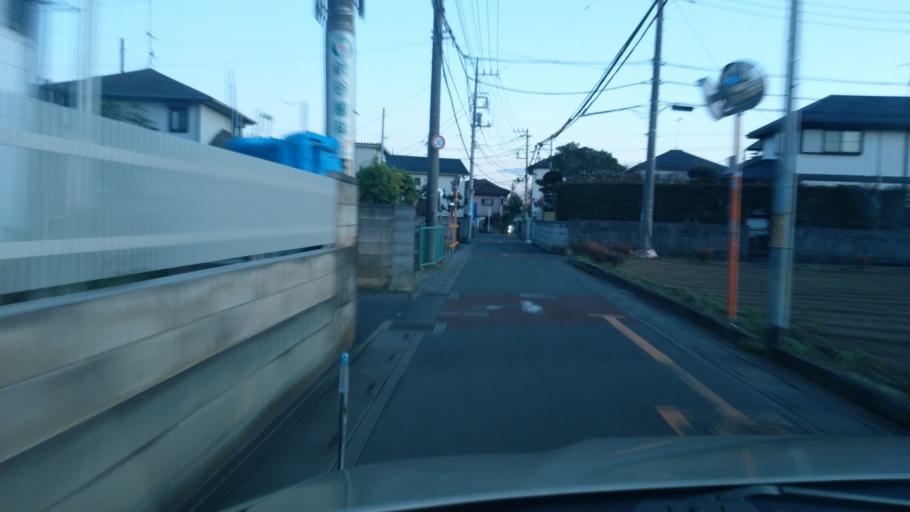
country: JP
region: Saitama
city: Yono
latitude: 35.9146
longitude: 139.5848
